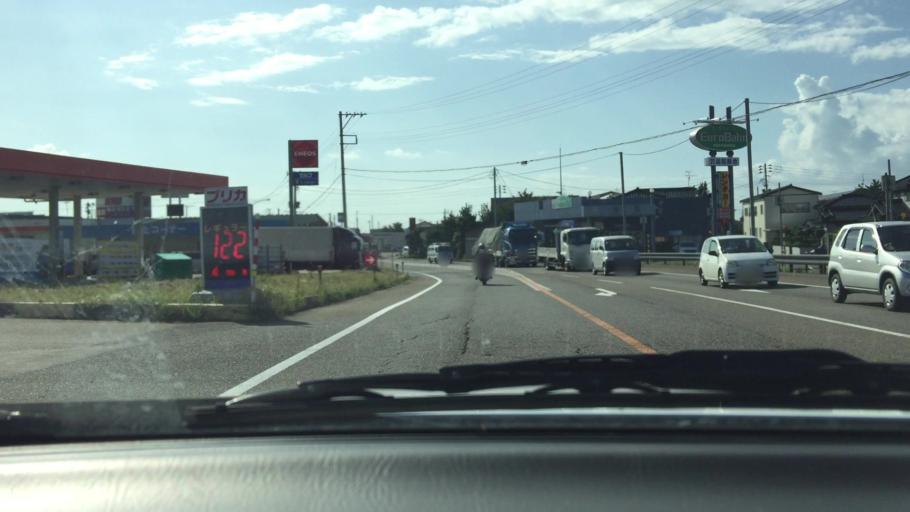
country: JP
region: Niigata
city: Kashiwazaki
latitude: 37.3887
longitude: 138.5906
